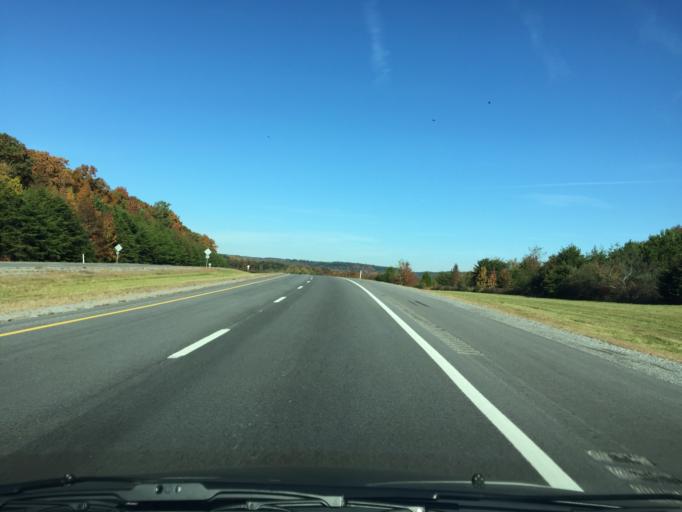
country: US
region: Tennessee
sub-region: Hamilton County
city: Sale Creek
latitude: 35.3396
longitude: -85.1675
